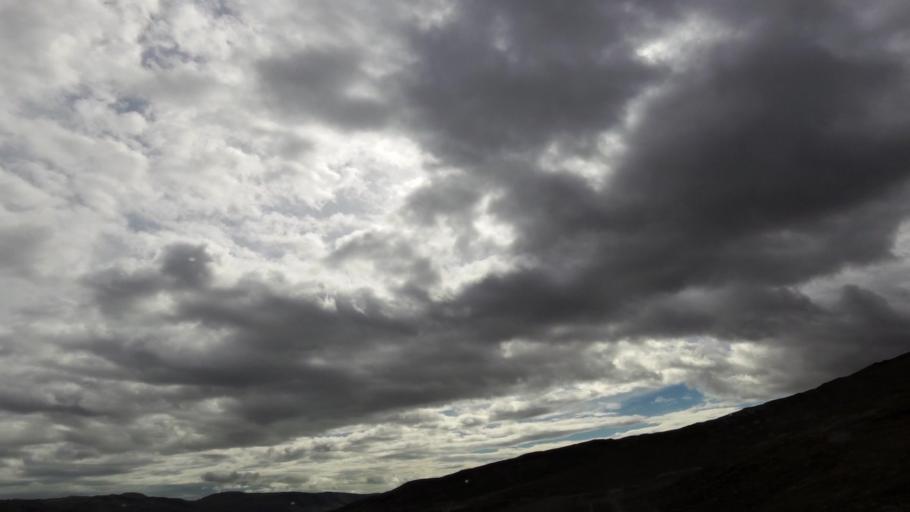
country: IS
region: West
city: Stykkisholmur
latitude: 65.5919
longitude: -22.1330
